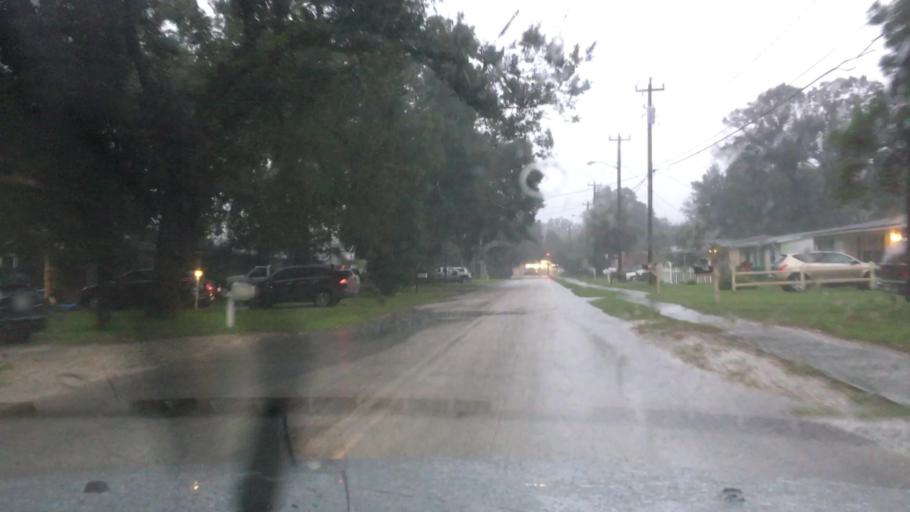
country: US
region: Florida
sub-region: Volusia County
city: Holly Hill
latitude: 29.2251
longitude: -81.0408
